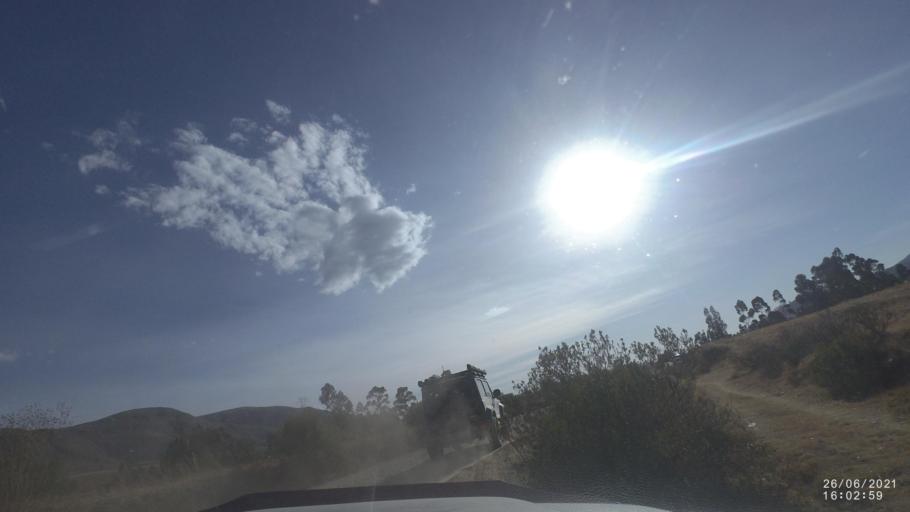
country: BO
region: Cochabamba
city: Arani
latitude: -17.8365
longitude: -65.7500
